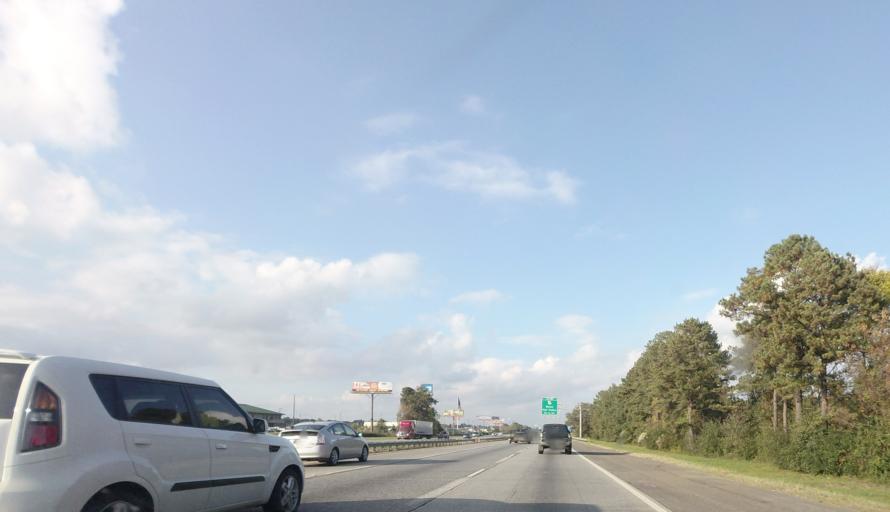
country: US
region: Georgia
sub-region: Peach County
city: Byron
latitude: 32.6494
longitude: -83.7438
